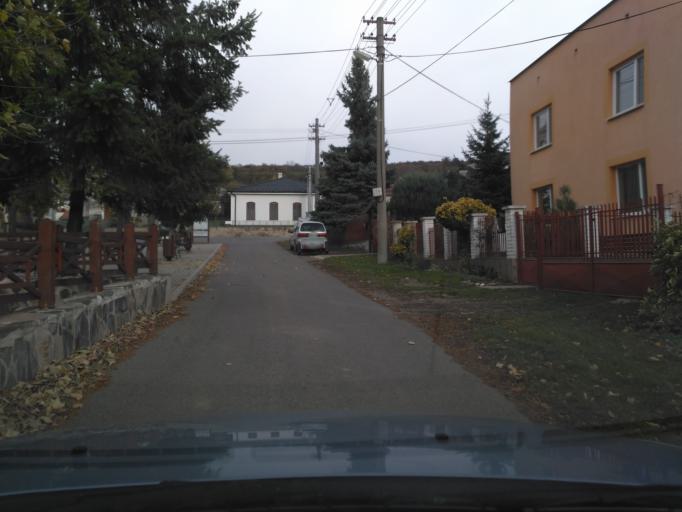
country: HU
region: Borsod-Abauj-Zemplen
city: Satoraljaujhely
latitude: 48.4393
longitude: 21.7330
